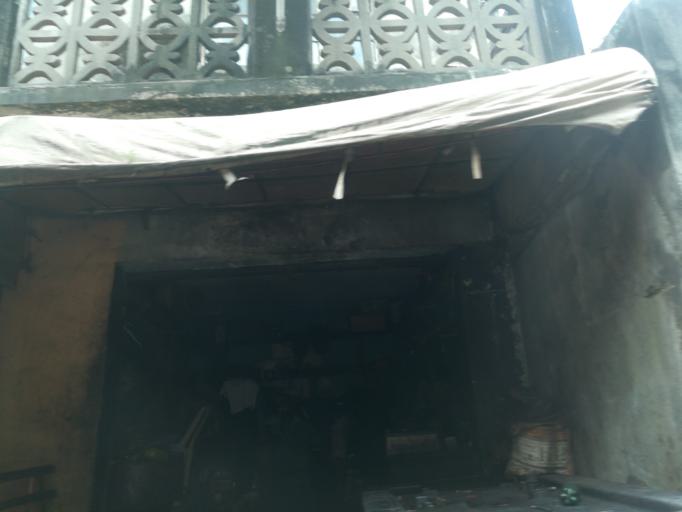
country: NG
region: Lagos
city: Mushin
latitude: 6.5275
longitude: 3.3667
